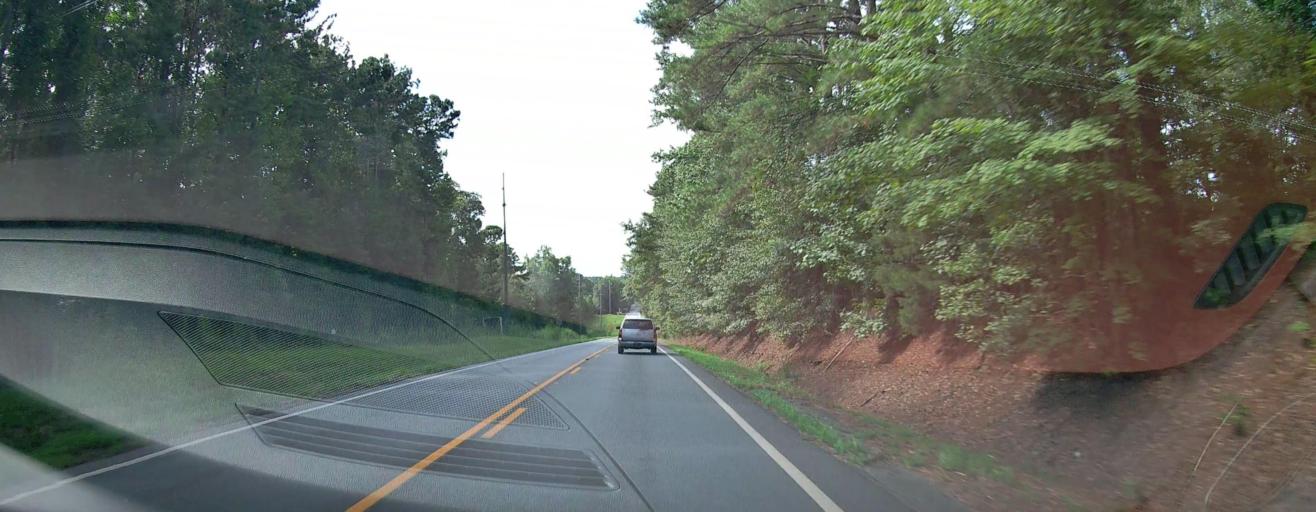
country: US
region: Georgia
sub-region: Upson County
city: Hannahs Mill
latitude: 32.9786
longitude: -84.4964
